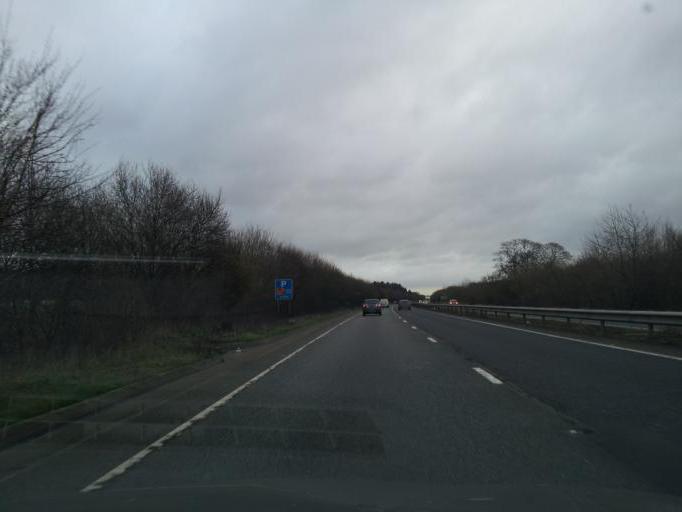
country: GB
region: England
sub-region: Norfolk
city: Thorpe Hamlet
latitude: 52.6161
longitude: 1.3406
